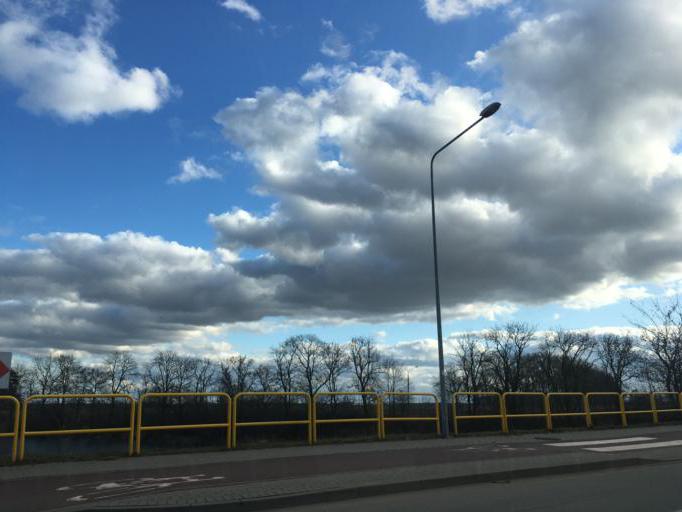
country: PL
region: Pomeranian Voivodeship
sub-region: Powiat nowodworski
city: Ostaszewo
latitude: 54.3096
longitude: 18.9248
